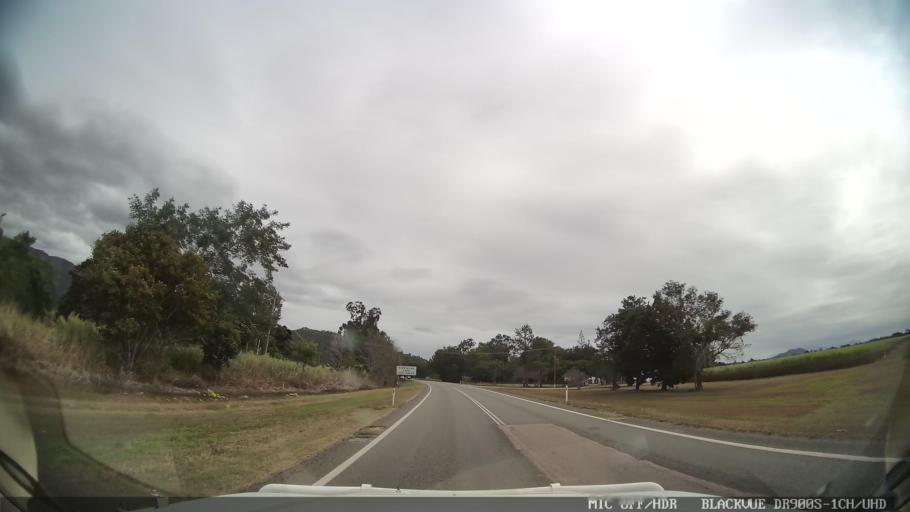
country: AU
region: Queensland
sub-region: Hinchinbrook
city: Ingham
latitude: -18.8642
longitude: 146.1754
